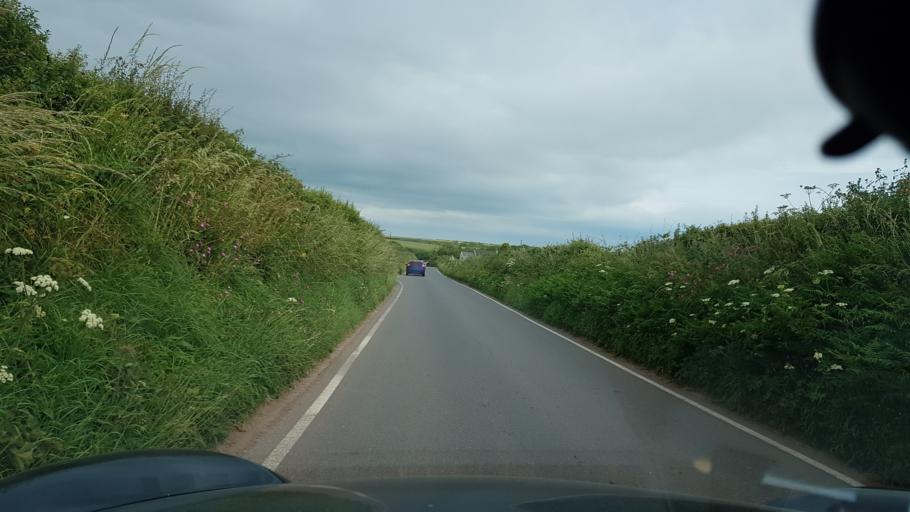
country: GB
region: Wales
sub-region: Pembrokeshire
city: Dale
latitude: 51.7500
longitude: -5.1398
